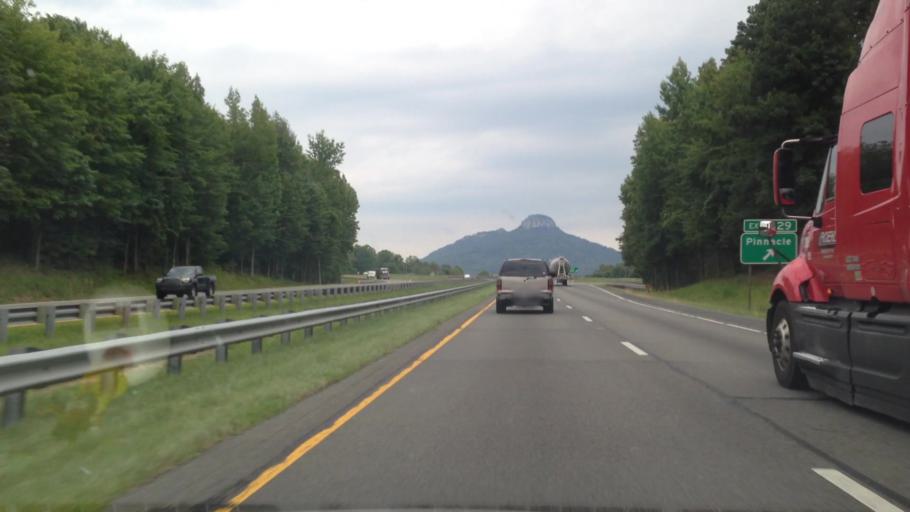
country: US
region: North Carolina
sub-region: Surry County
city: Pilot Mountain
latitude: 36.3145
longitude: -80.4341
